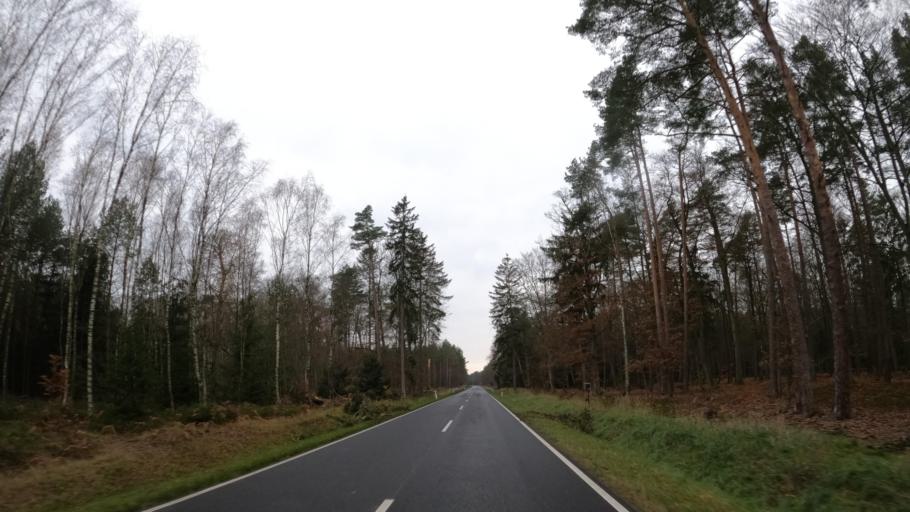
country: PL
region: West Pomeranian Voivodeship
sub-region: Powiat policki
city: Nowe Warpno
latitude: 53.6671
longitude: 14.4308
